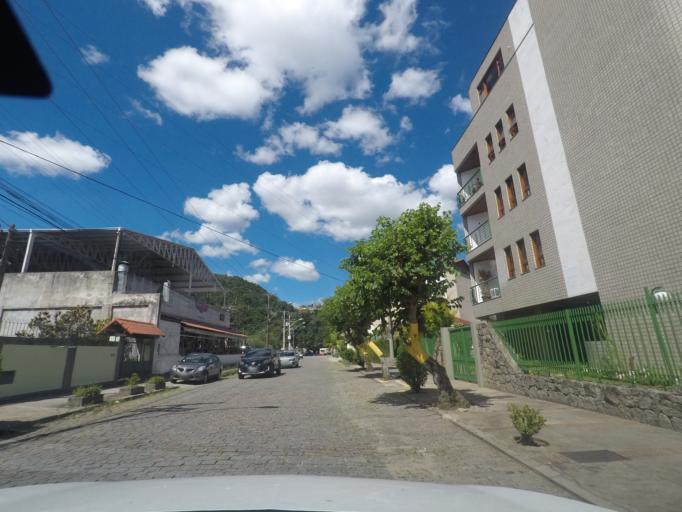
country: BR
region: Rio de Janeiro
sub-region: Teresopolis
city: Teresopolis
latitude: -22.4348
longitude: -42.9758
